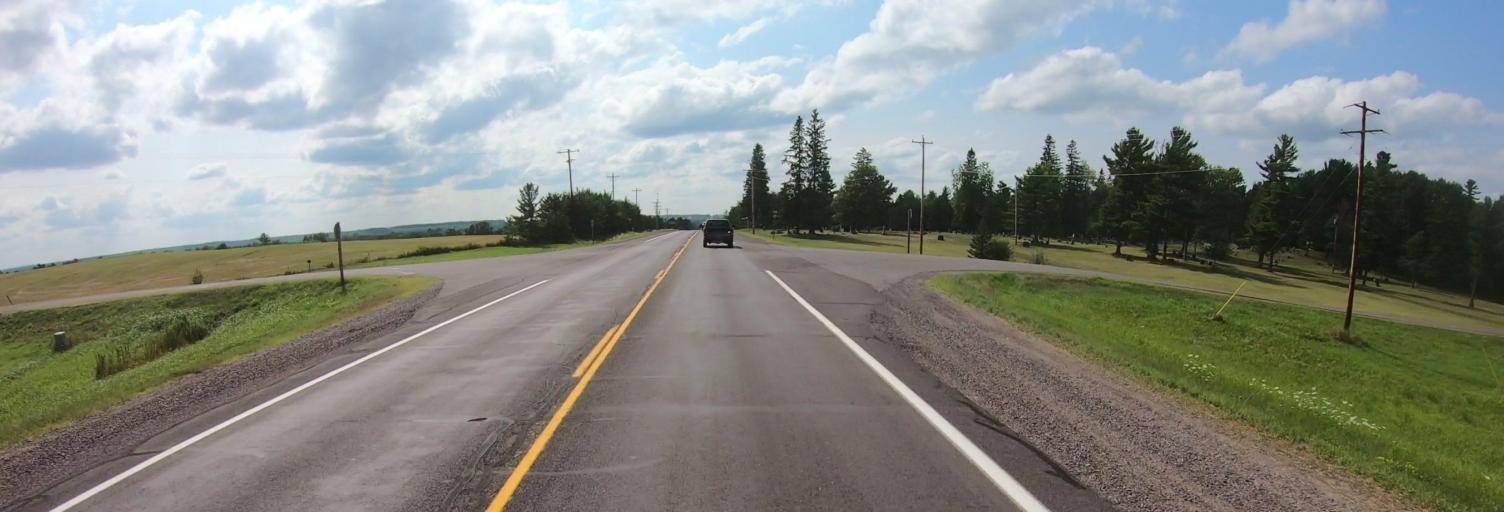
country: US
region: Michigan
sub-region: Ontonagon County
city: Ontonagon
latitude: 46.5348
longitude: -89.2610
